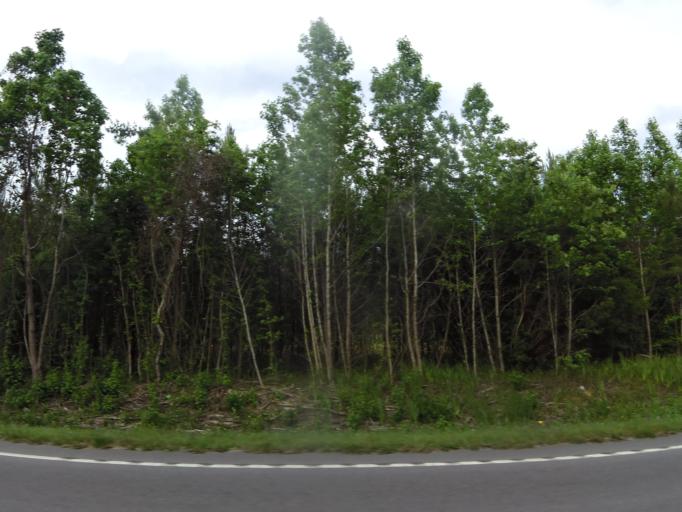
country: US
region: South Carolina
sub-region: Jasper County
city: Ridgeland
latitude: 32.4766
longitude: -81.1146
